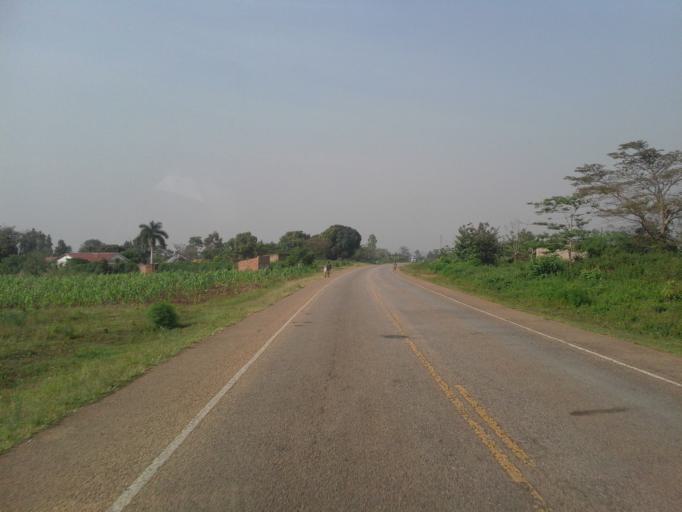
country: UG
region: Eastern Region
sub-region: Mbale District
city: Mbale
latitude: 1.0571
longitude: 34.0707
